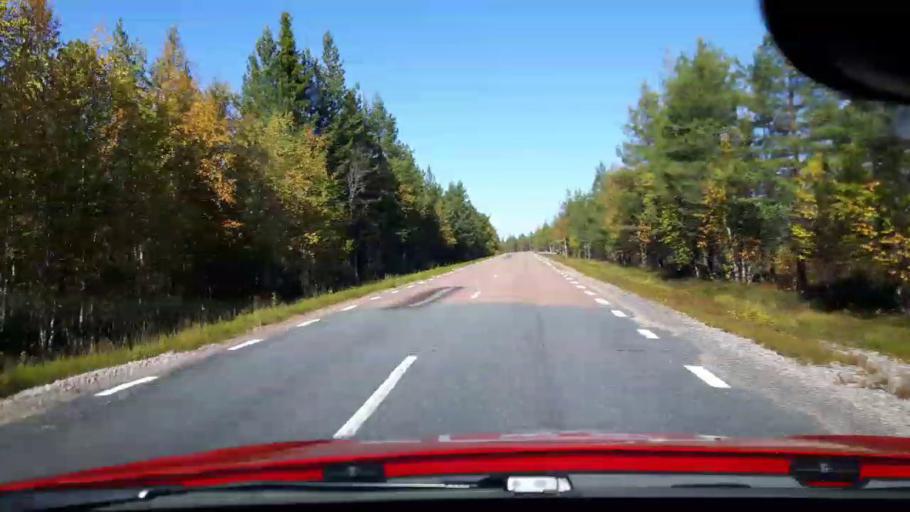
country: SE
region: Jaemtland
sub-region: Harjedalens Kommun
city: Sveg
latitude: 61.7365
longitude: 14.1633
